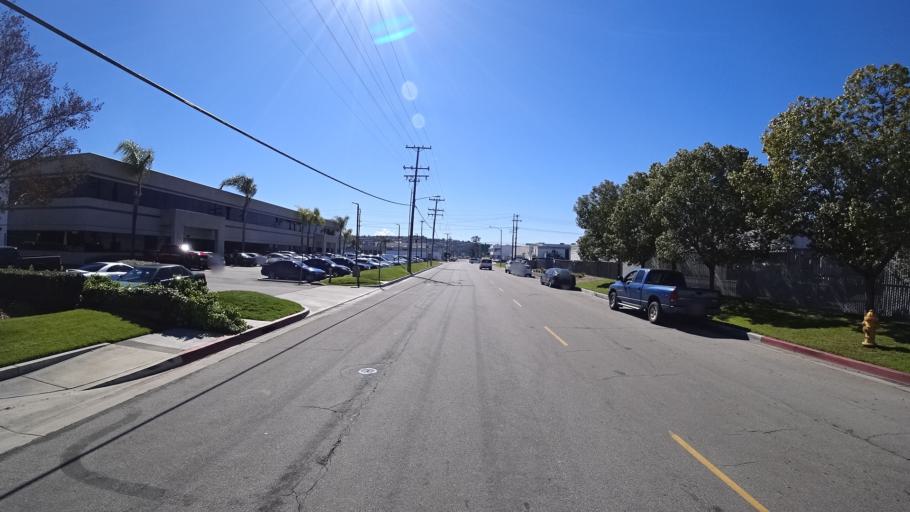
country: US
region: California
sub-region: Orange County
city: Yorba Linda
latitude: 33.8605
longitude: -117.8234
